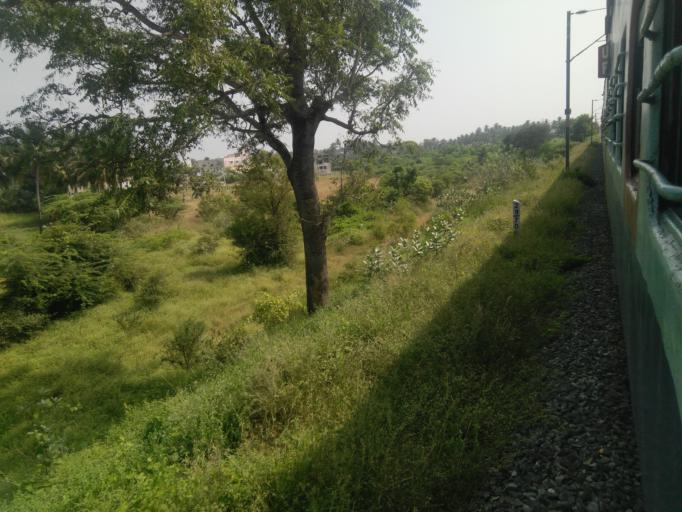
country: IN
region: Tamil Nadu
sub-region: Coimbatore
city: Mettupalayam
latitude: 11.2726
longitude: 76.9450
